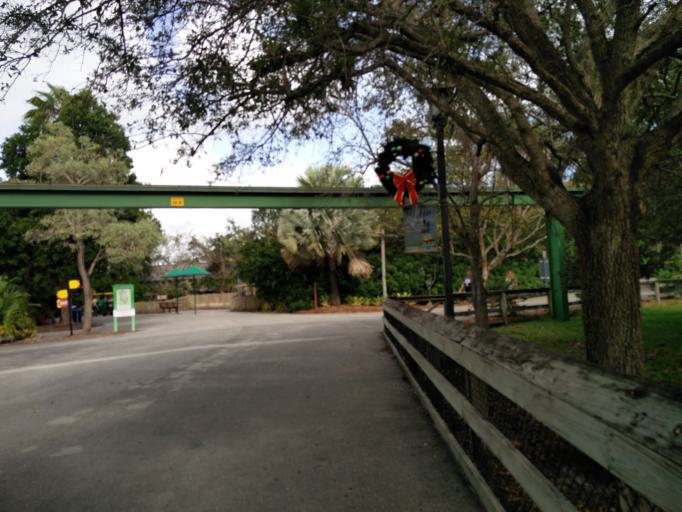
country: US
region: Florida
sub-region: Miami-Dade County
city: South Miami Heights
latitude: 25.6087
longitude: -80.3976
